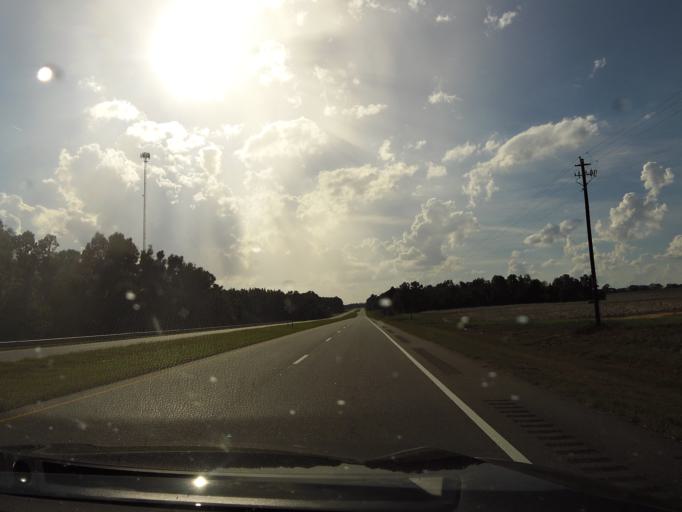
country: US
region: Georgia
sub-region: Brooks County
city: Quitman
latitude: 30.7855
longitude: -83.6058
